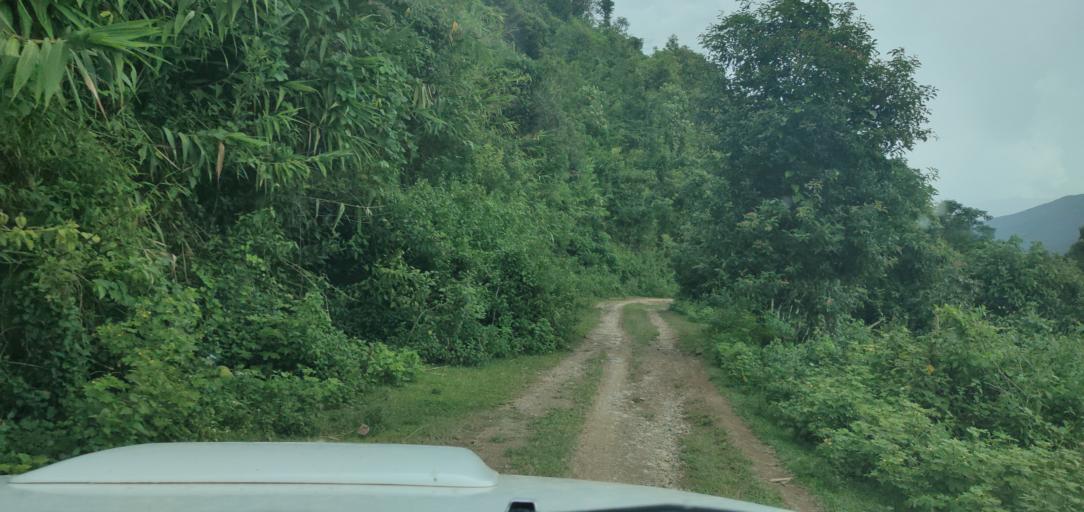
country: LA
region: Phongsali
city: Phongsali
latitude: 21.4417
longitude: 102.3284
